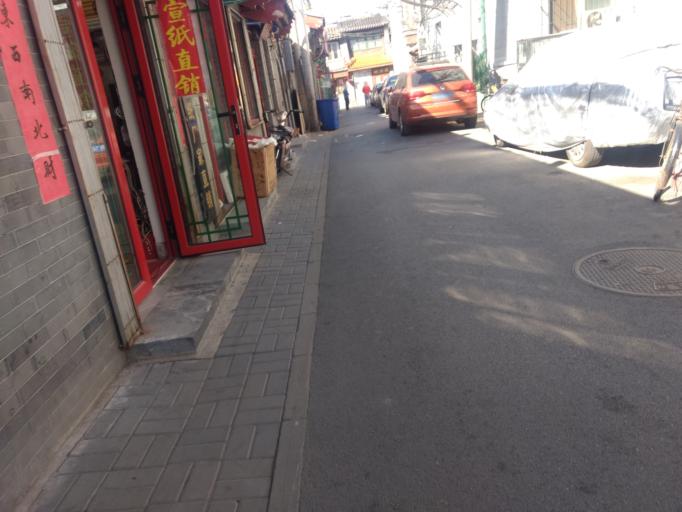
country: CN
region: Beijing
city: Beijing
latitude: 39.8933
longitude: 116.3817
